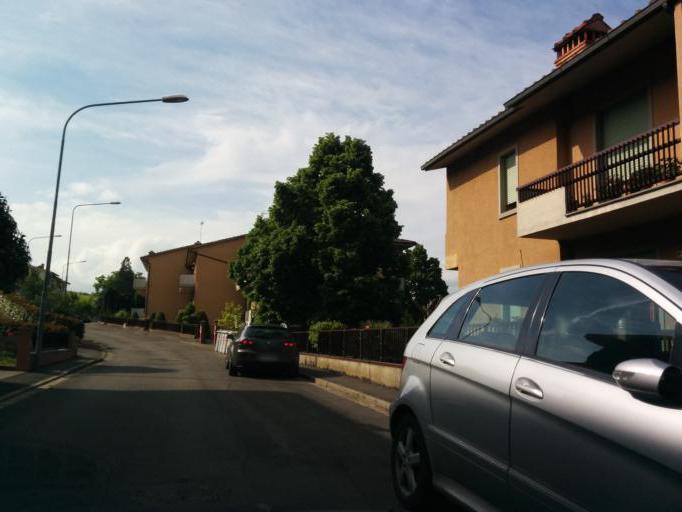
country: IT
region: Tuscany
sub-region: Province of Florence
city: Mercatale
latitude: 43.6159
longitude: 11.1908
